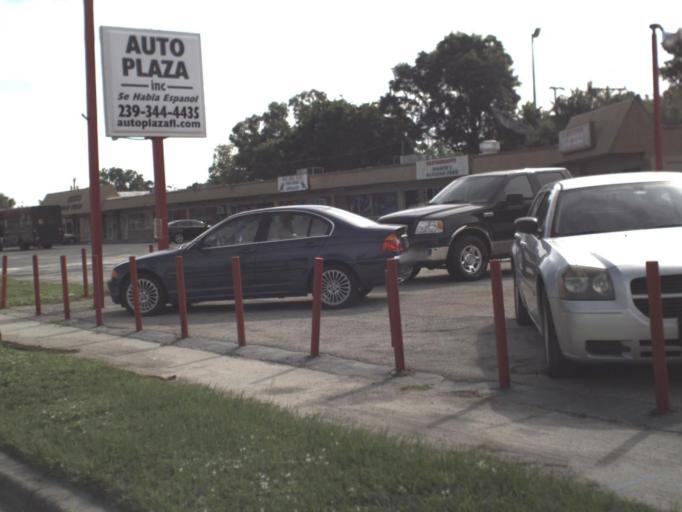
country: US
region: Florida
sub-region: Lee County
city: Tice
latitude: 26.6595
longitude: -81.8426
